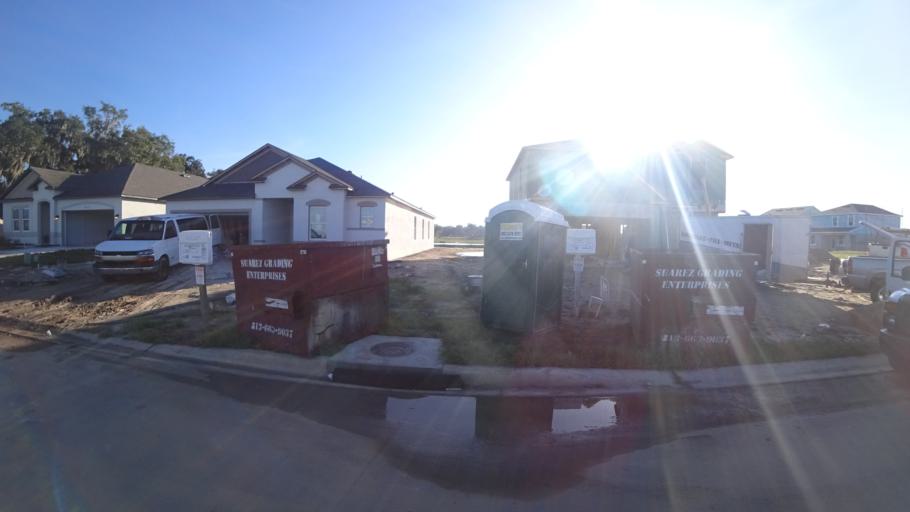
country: US
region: Florida
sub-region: Manatee County
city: Ellenton
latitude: 27.5572
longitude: -82.5223
